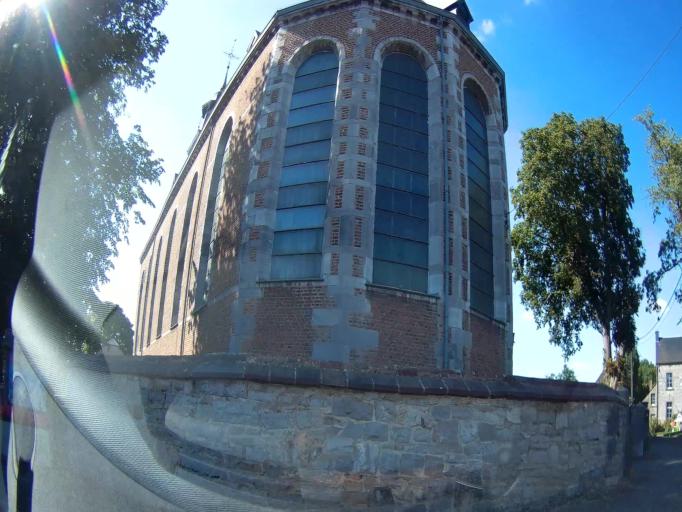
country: BE
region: Wallonia
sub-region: Province de Namur
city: Houyet
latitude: 50.2472
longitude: 4.9902
